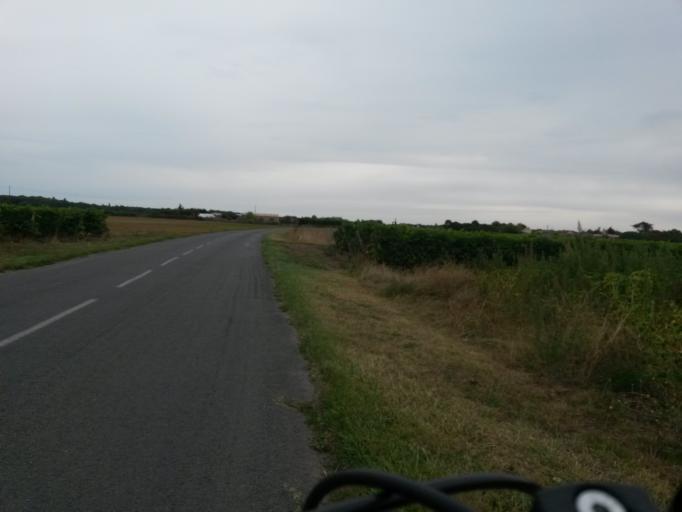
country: FR
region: Poitou-Charentes
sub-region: Departement de la Charente-Maritime
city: Dolus-d'Oleron
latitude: 45.9387
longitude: -1.3424
